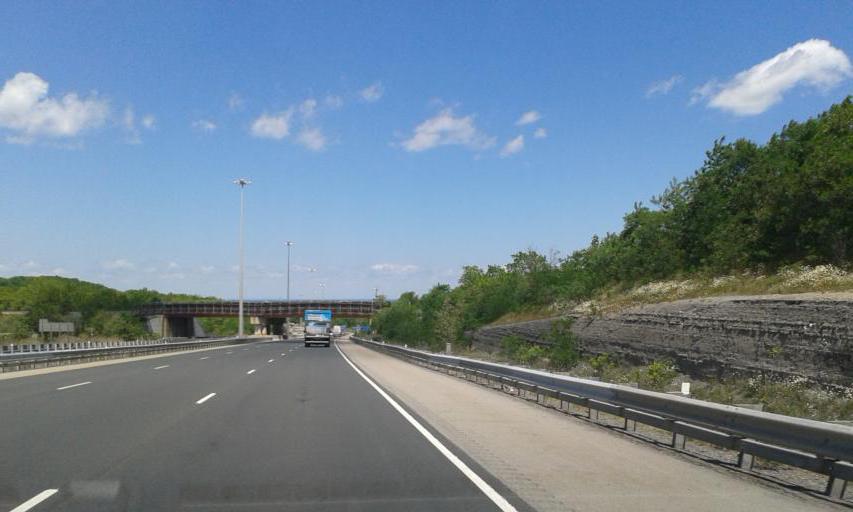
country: CA
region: Ontario
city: Thorold
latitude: 43.1434
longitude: -79.1397
